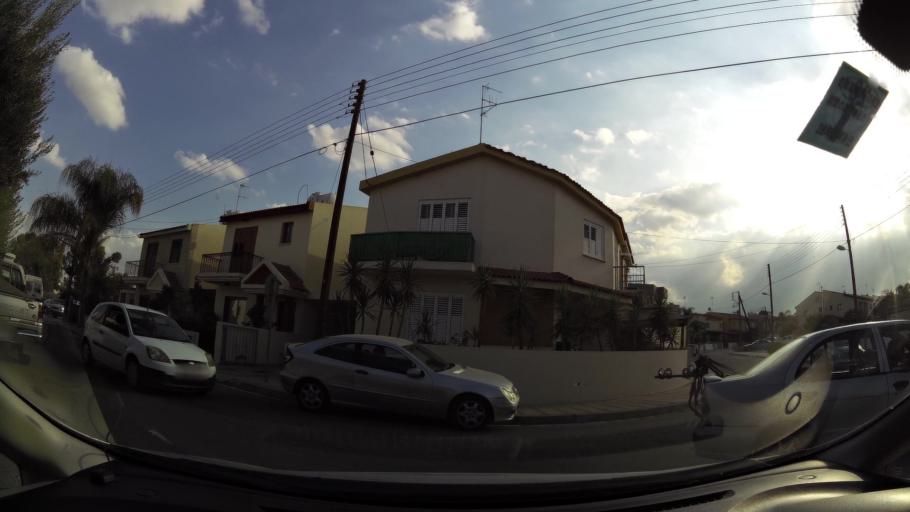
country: CY
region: Lefkosia
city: Kato Deftera
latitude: 35.1077
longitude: 33.2888
